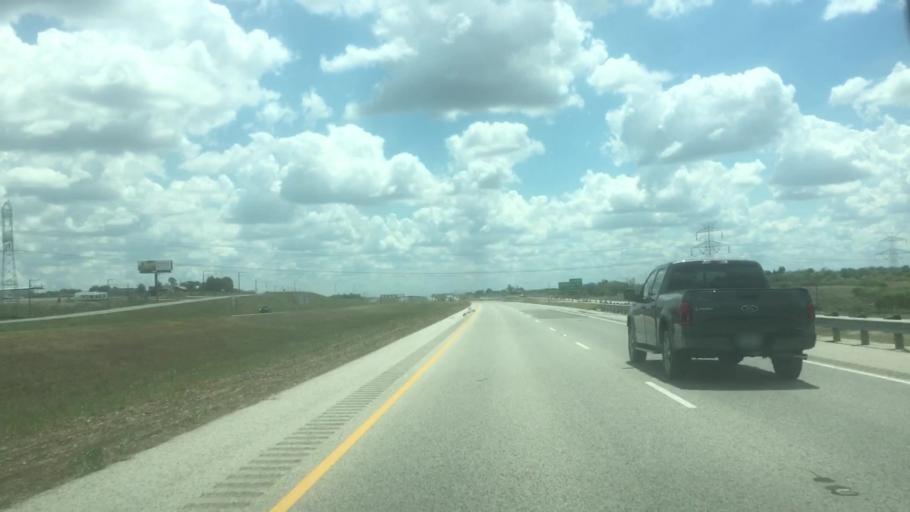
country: US
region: Texas
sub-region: Caldwell County
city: Uhland
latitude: 29.9982
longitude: -97.6864
